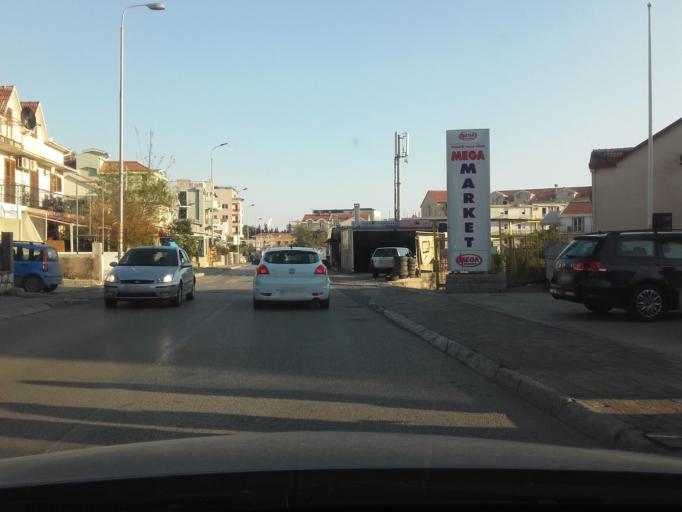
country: ME
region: Budva
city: Budva
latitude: 42.2904
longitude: 18.8507
